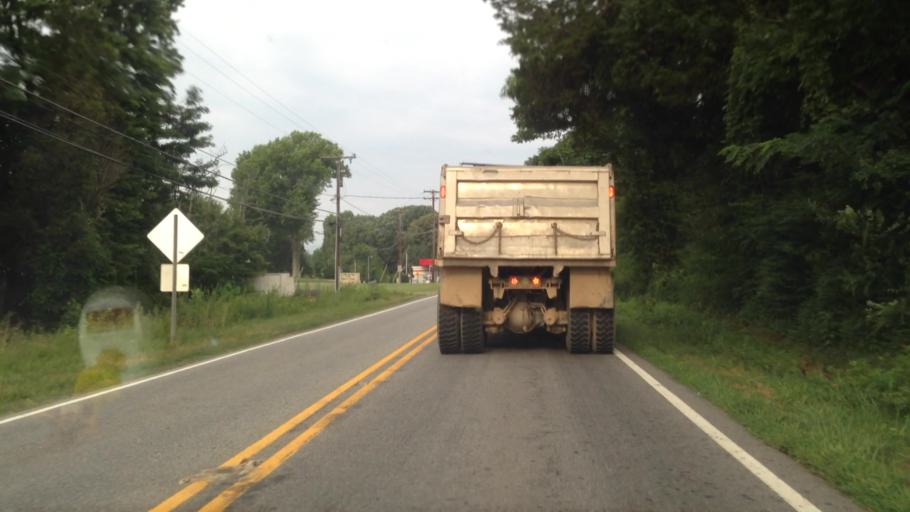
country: US
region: North Carolina
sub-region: Forsyth County
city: Walkertown
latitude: 36.1908
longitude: -80.2184
